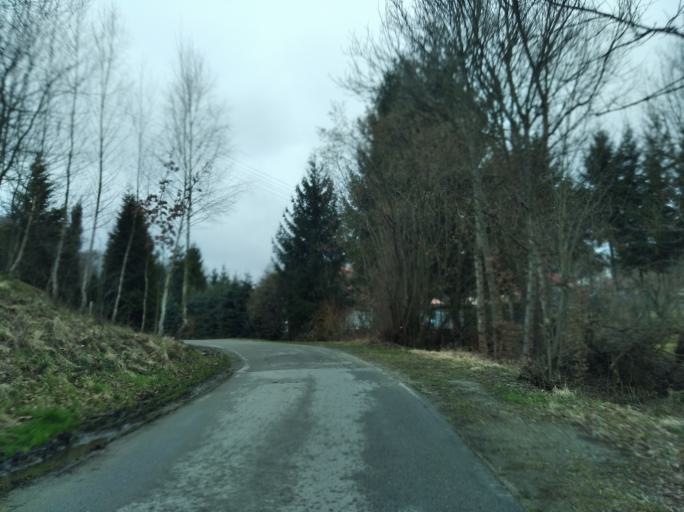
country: PL
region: Subcarpathian Voivodeship
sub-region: Powiat strzyzowski
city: Strzyzow
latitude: 49.8931
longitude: 21.8193
